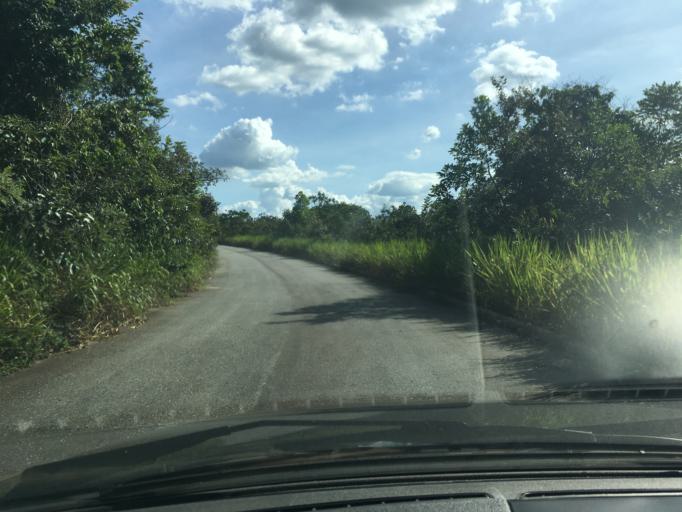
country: BR
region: Minas Gerais
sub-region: Ibirite
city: Ibirite
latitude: -20.1274
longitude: -44.0695
